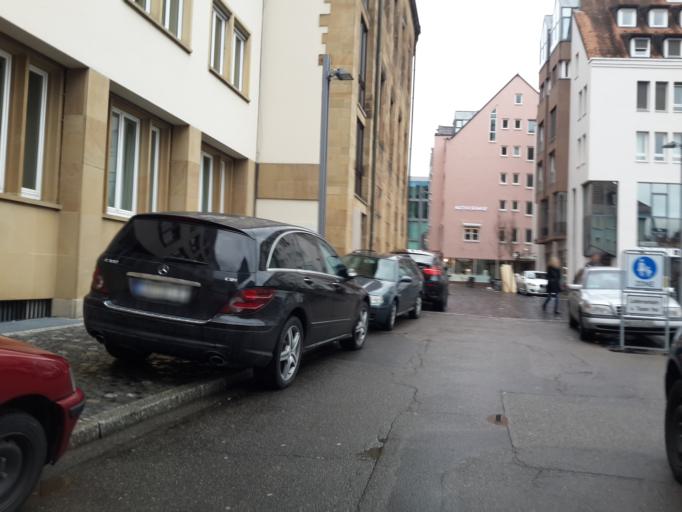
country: DE
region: Baden-Wuerttemberg
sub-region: Regierungsbezirk Stuttgart
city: Heilbronn
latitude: 49.1430
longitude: 9.2183
